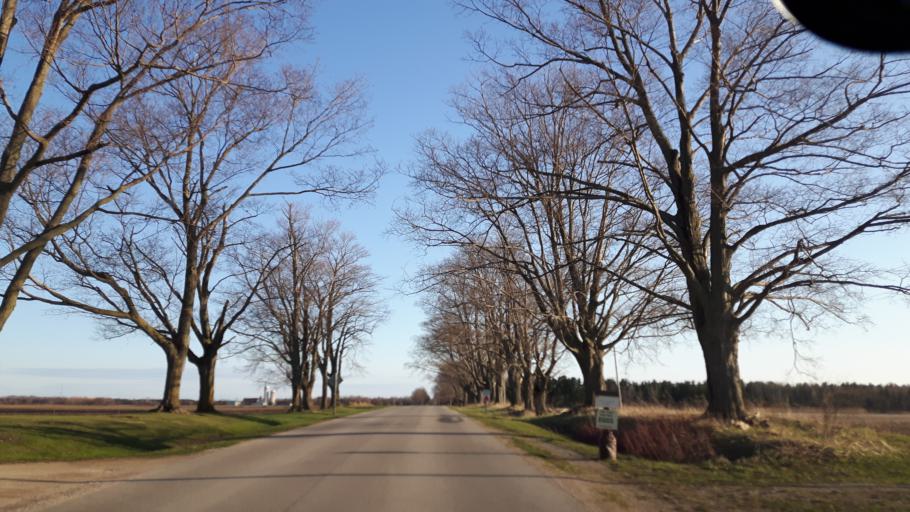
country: CA
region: Ontario
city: Goderich
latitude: 43.6403
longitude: -81.6846
